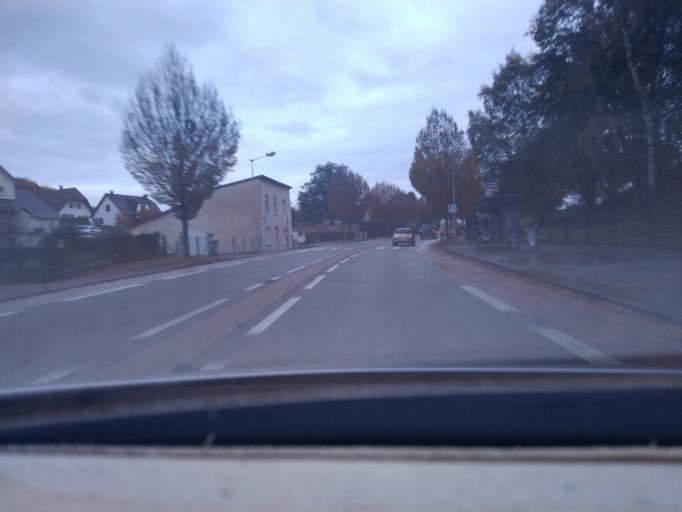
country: FR
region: Haute-Normandie
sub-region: Departement de la Seine-Maritime
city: Canteleu
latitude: 49.4446
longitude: 1.0152
